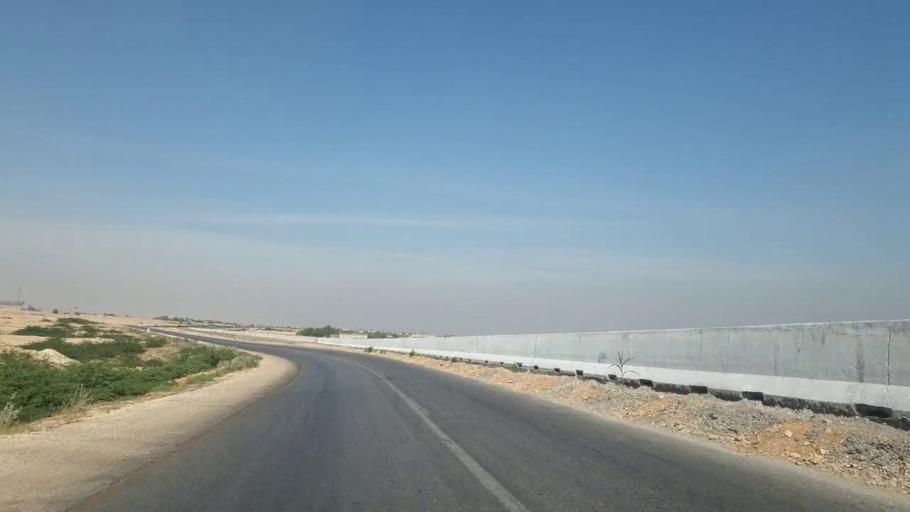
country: PK
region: Sindh
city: Matiari
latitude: 25.6814
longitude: 68.2963
